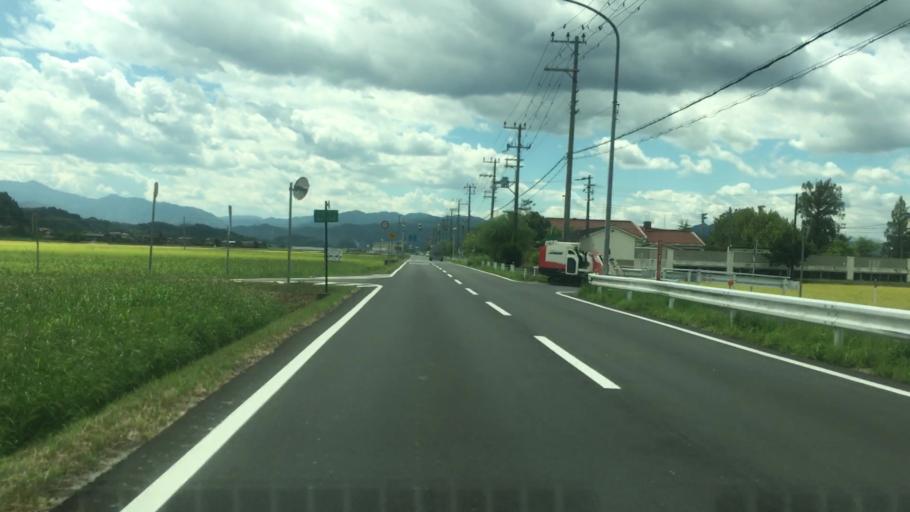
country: JP
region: Hyogo
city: Toyooka
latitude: 35.5312
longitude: 134.8398
